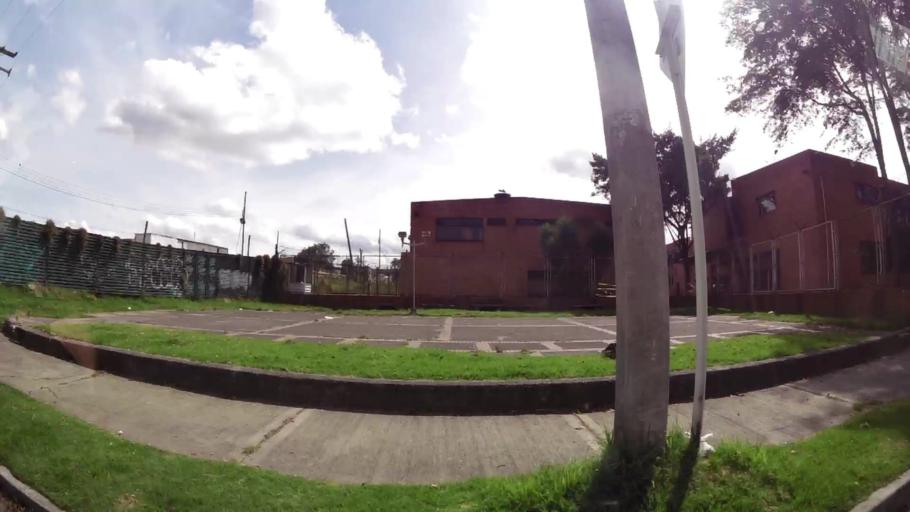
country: CO
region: Bogota D.C.
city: Bogota
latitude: 4.6456
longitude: -74.1332
